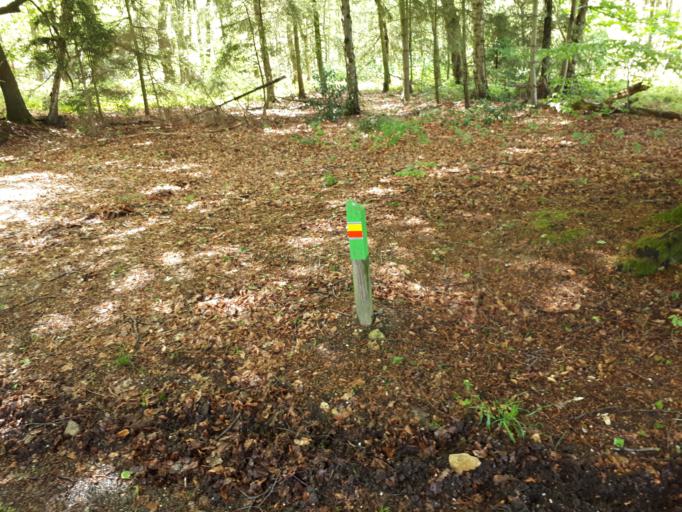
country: BE
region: Wallonia
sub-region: Province de Liege
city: Plombieres
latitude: 50.7668
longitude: 5.9798
